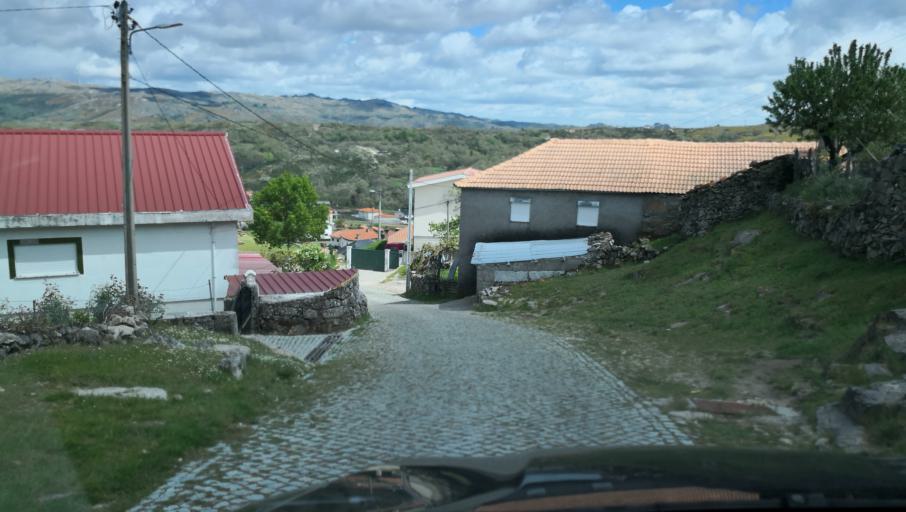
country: PT
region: Vila Real
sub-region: Vila Real
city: Vila Real
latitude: 41.4082
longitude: -7.7173
